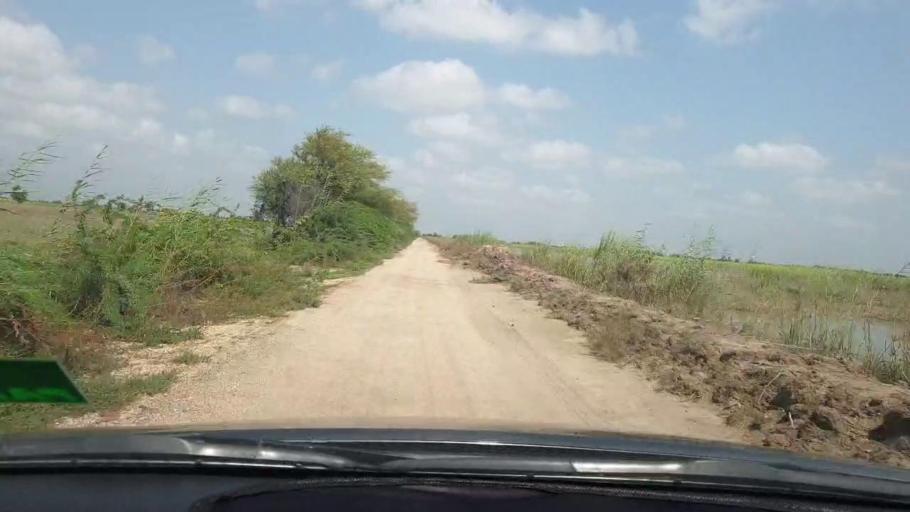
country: PK
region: Sindh
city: Tando Bago
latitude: 24.8573
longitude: 69.0354
